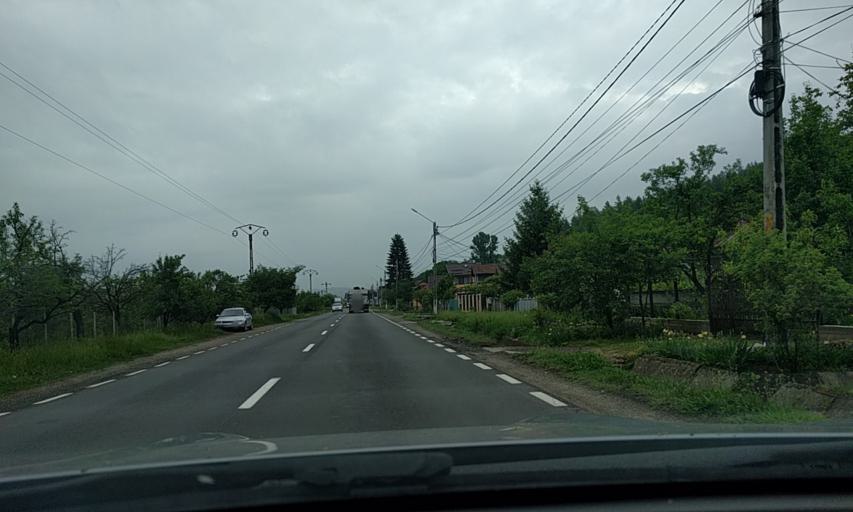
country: RO
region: Dambovita
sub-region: Comuna Vulcana-Pandele
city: Vulcana-Pandele
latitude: 45.0102
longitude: 25.4032
